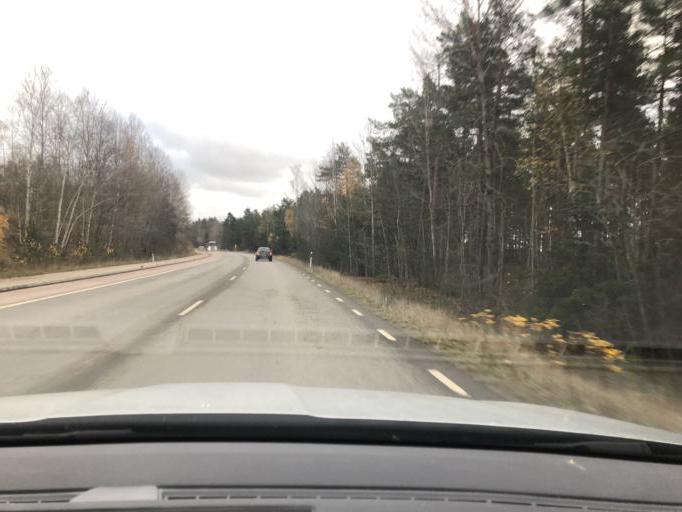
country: SE
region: Soedermanland
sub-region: Strangnas Kommun
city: Strangnas
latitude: 59.3690
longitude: 17.0089
